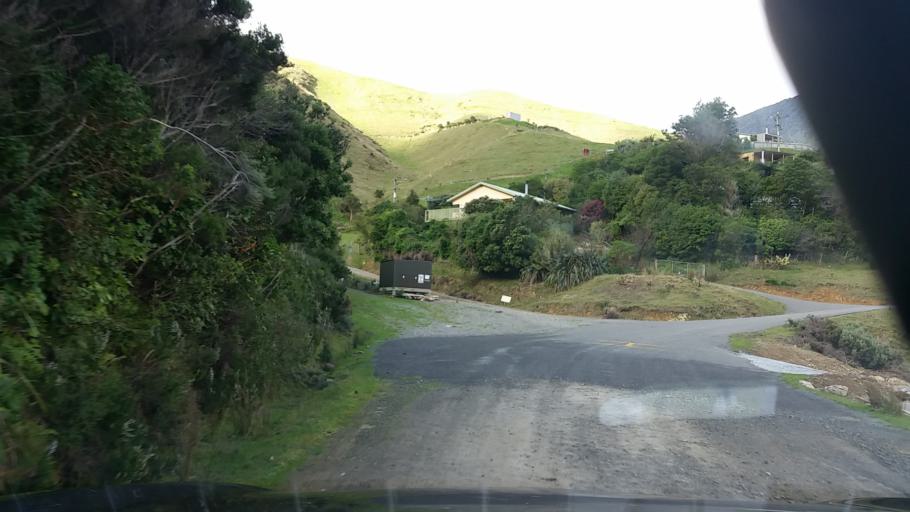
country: NZ
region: Marlborough
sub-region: Marlborough District
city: Picton
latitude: -40.9885
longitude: 173.8281
